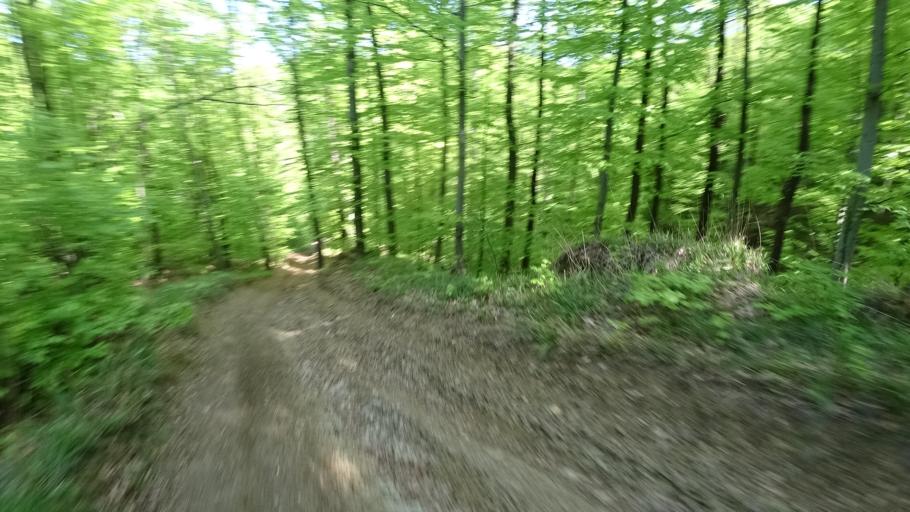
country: HR
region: Zagrebacka
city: Jablanovec
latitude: 45.8647
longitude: 15.8944
